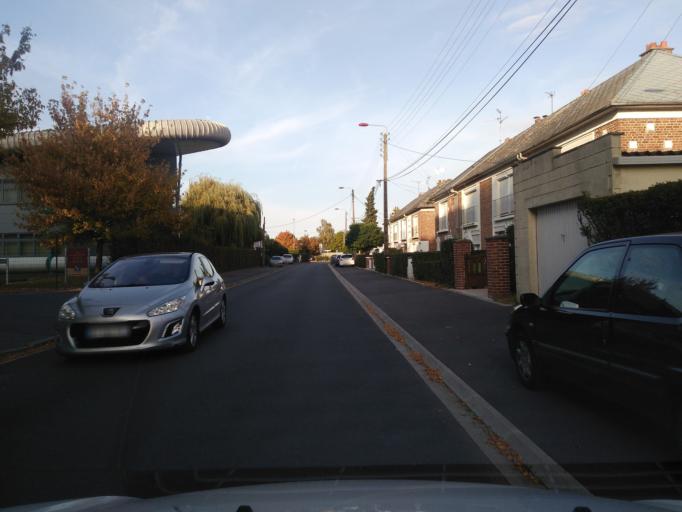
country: FR
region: Nord-Pas-de-Calais
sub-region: Departement du Nord
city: Onnaing
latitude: 50.3823
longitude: 3.5830
